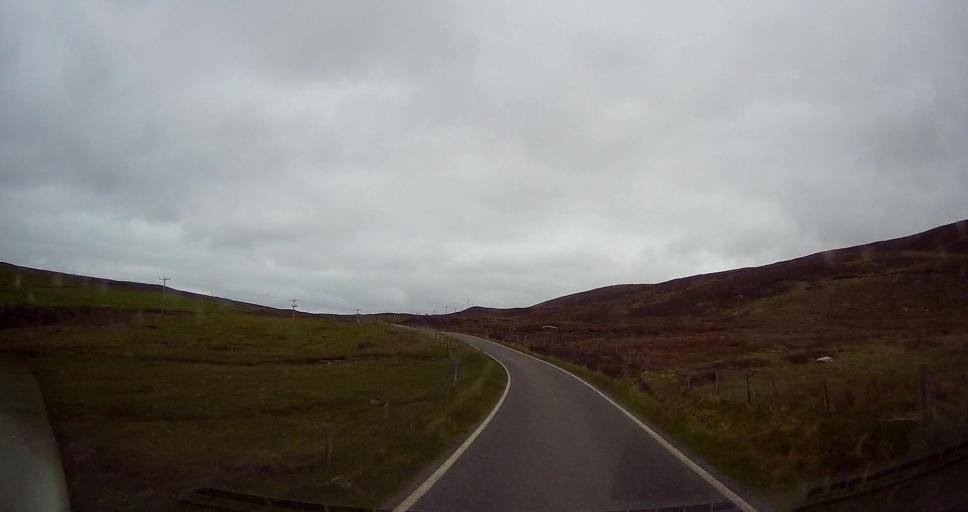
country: GB
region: Scotland
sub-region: Shetland Islands
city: Lerwick
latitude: 60.3060
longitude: -1.3380
